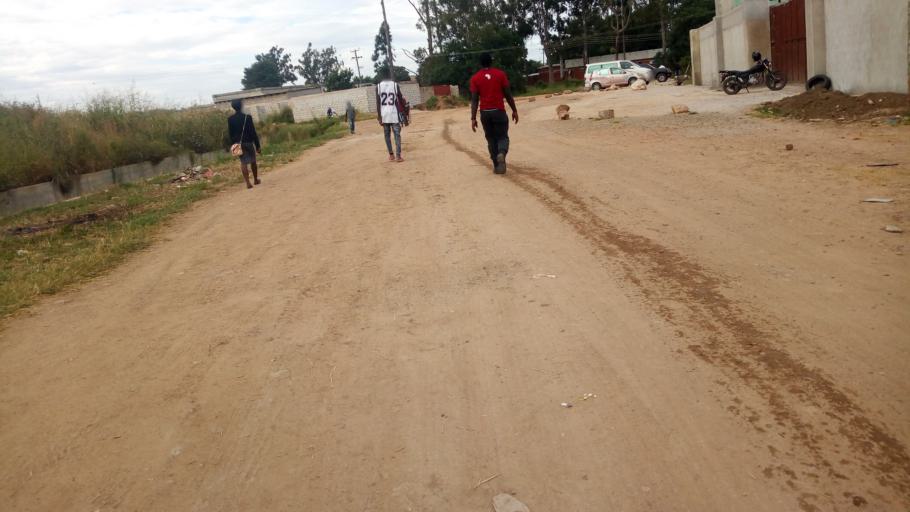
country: ZM
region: Lusaka
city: Lusaka
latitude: -15.3928
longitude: 28.2854
